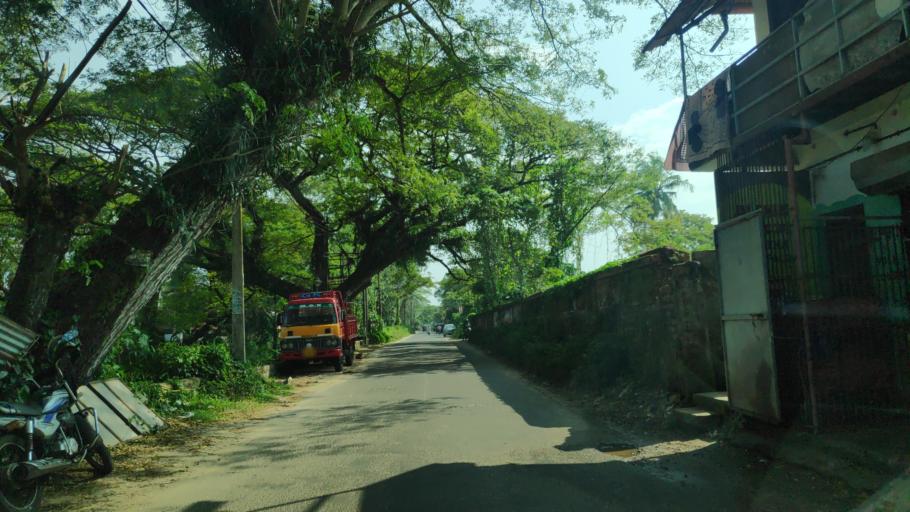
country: IN
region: Kerala
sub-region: Alappuzha
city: Alleppey
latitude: 9.4991
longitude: 76.3214
